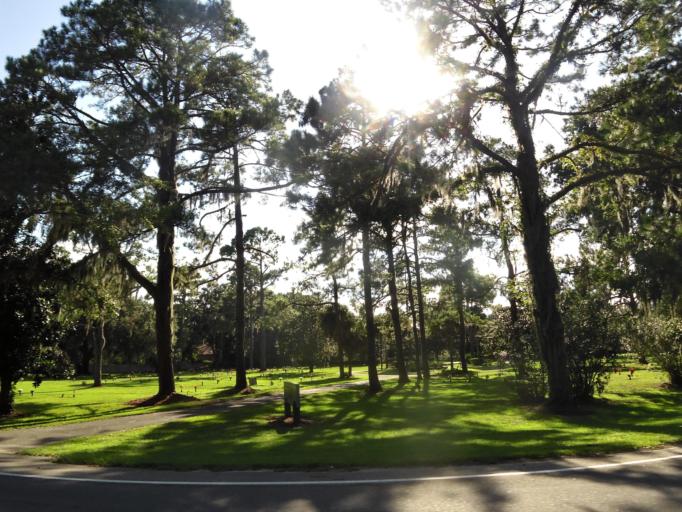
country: US
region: Georgia
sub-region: Glynn County
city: Saint Simon Mills
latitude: 31.2159
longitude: -81.3753
